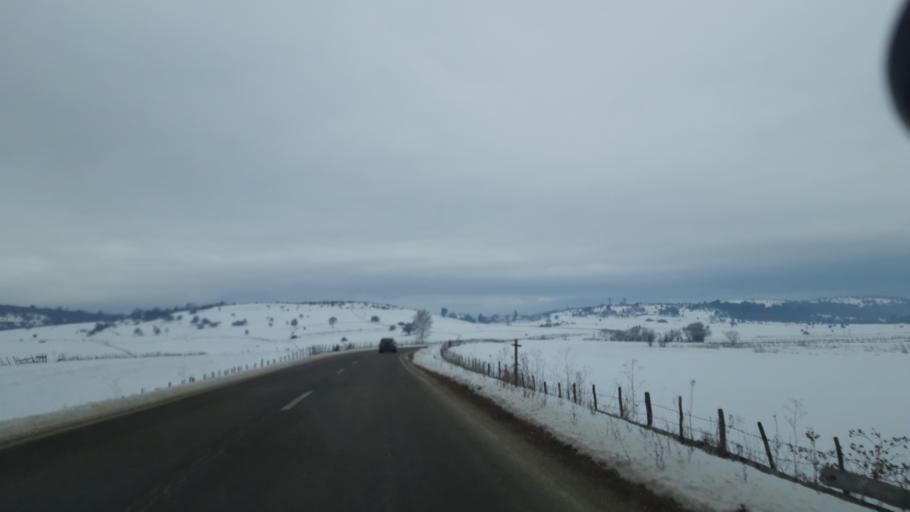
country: BA
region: Republika Srpska
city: Sokolac
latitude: 43.9560
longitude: 18.8500
